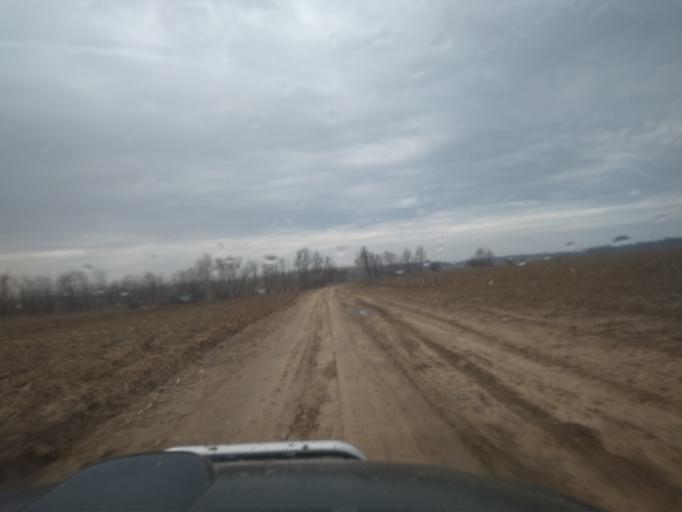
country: HU
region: Szabolcs-Szatmar-Bereg
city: Apagy
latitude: 47.9694
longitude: 21.9215
